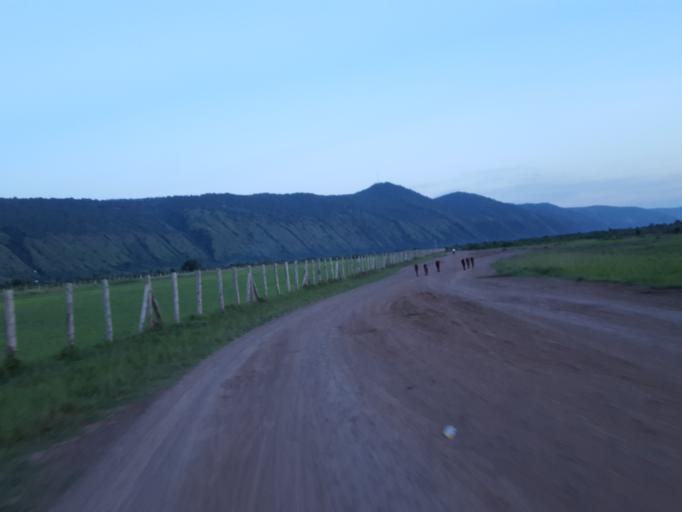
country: UG
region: Western Region
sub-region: Kibale District
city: Kagadi
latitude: 1.2437
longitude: 30.7471
